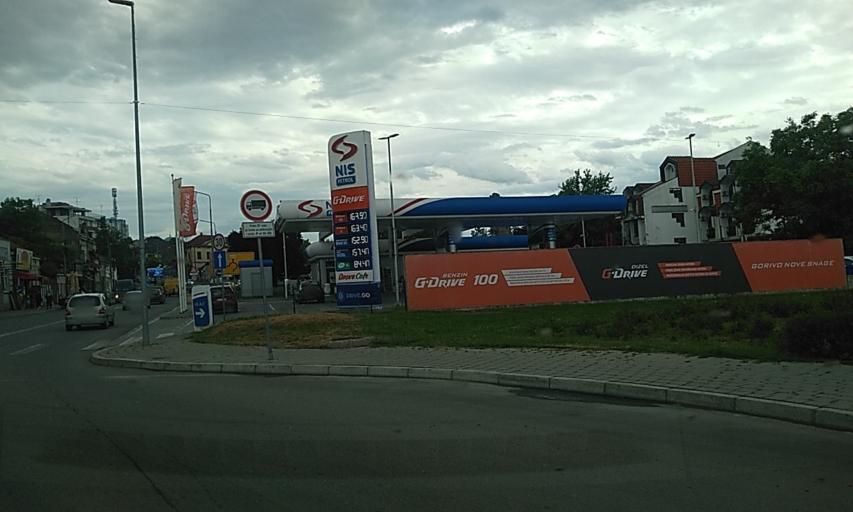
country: RS
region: Central Serbia
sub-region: Rasinski Okrug
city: Krusevac
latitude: 43.5865
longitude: 21.3222
